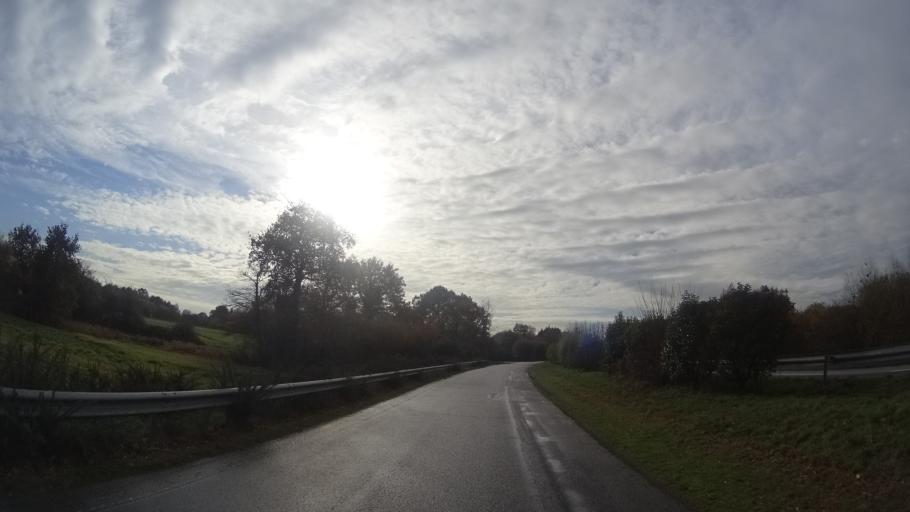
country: FR
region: Brittany
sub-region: Departement du Morbihan
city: Rieux
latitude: 47.6217
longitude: -2.1019
